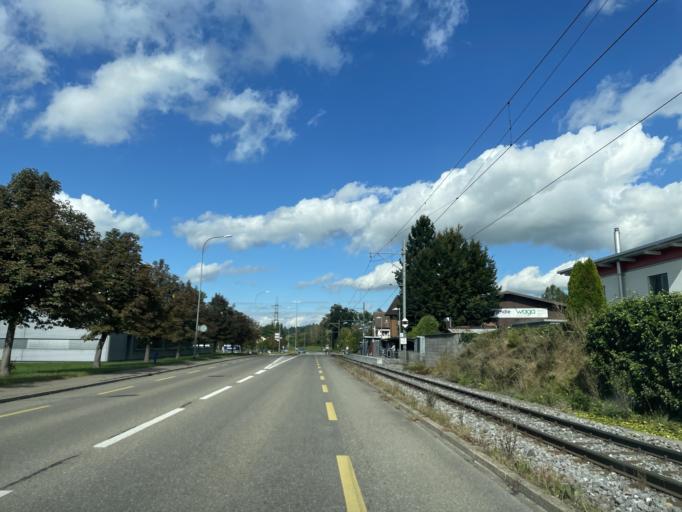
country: CH
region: Thurgau
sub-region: Muenchwilen District
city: Wangi
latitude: 47.5015
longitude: 8.9492
